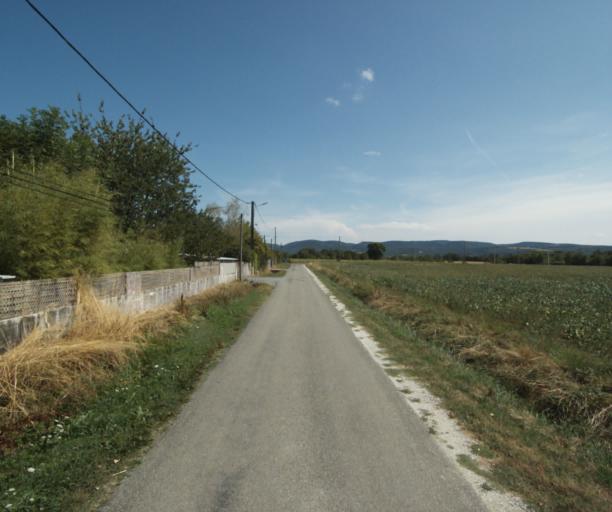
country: FR
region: Midi-Pyrenees
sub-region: Departement de la Haute-Garonne
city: Revel
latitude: 43.4830
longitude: 2.0059
